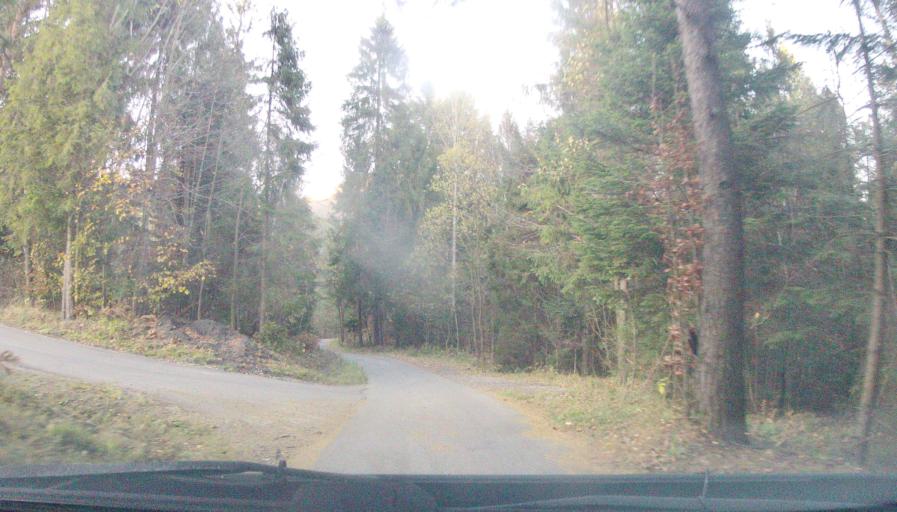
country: PL
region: Lesser Poland Voivodeship
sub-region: Powiat suski
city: Krzeszow
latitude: 49.7614
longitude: 19.4492
